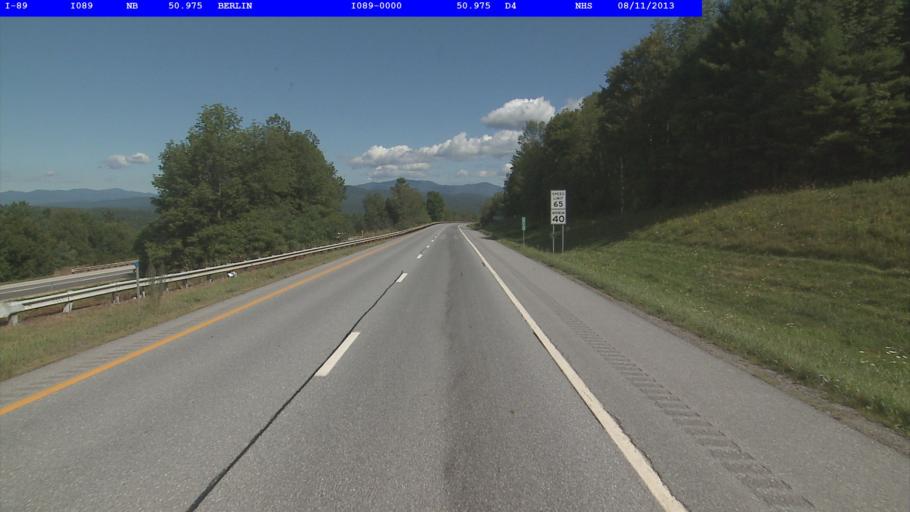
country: US
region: Vermont
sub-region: Washington County
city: Montpelier
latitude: 44.2253
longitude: -72.5856
